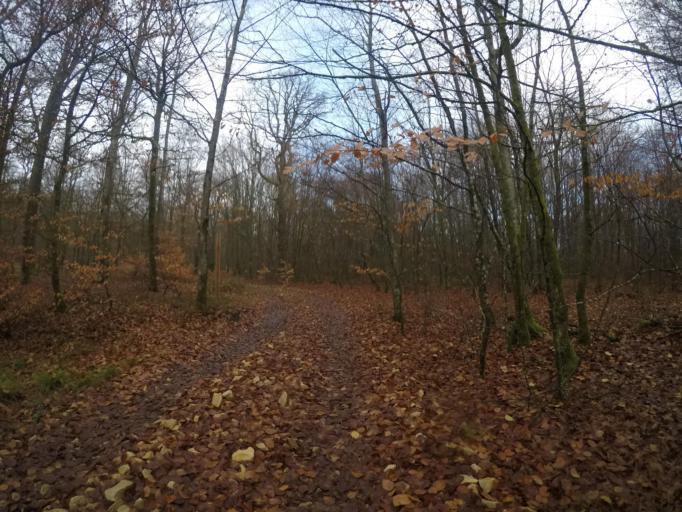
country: BE
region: Wallonia
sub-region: Province du Luxembourg
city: Habay-la-Vieille
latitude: 49.7413
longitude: 5.5935
